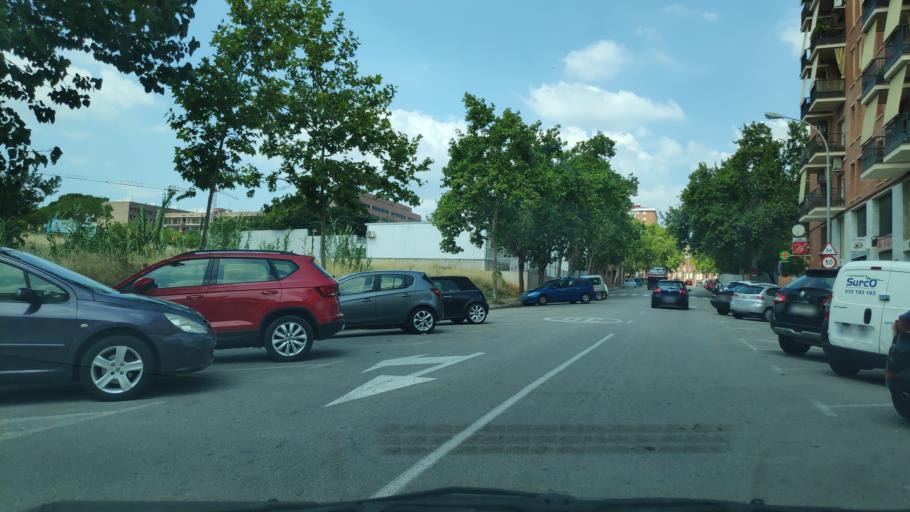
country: ES
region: Catalonia
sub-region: Provincia de Barcelona
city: Sant Quirze del Valles
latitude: 41.5460
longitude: 2.0861
